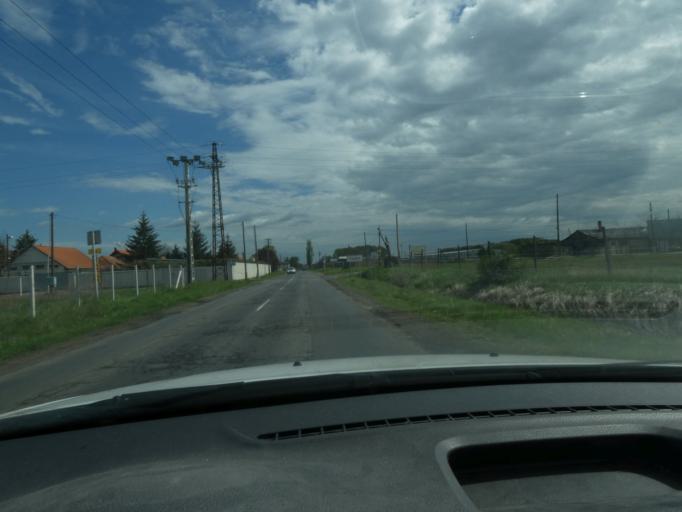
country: HU
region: Pest
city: Cegled
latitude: 47.1585
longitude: 19.7719
